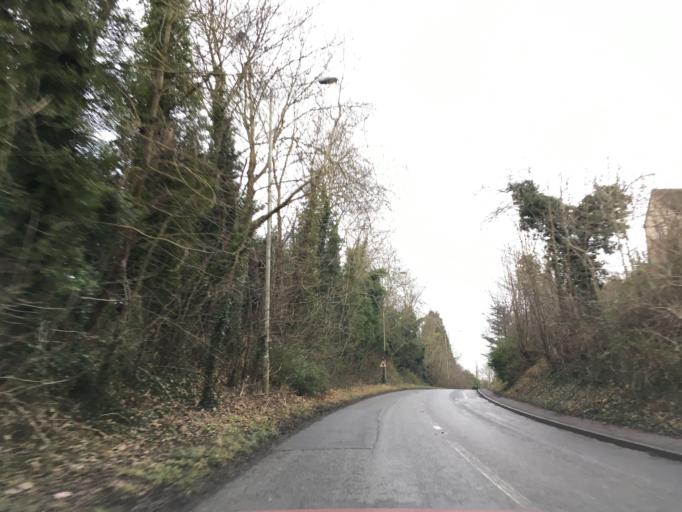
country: GB
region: England
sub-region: Gloucestershire
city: Cirencester
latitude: 51.7325
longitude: -1.9729
